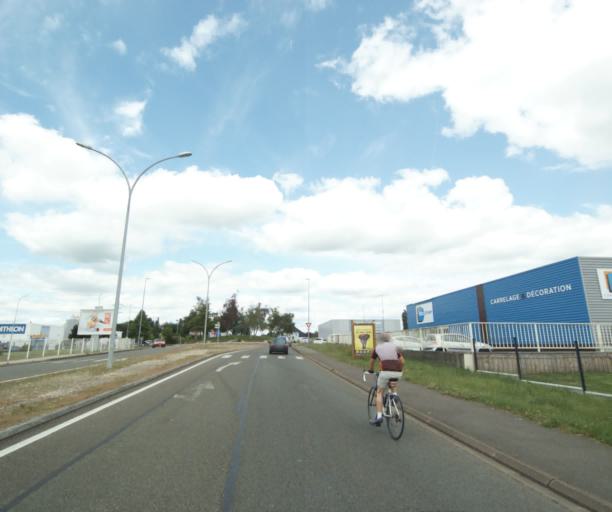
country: FR
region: Centre
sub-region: Departement d'Eure-et-Loir
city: Mainvilliers
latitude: 48.4465
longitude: 1.4513
